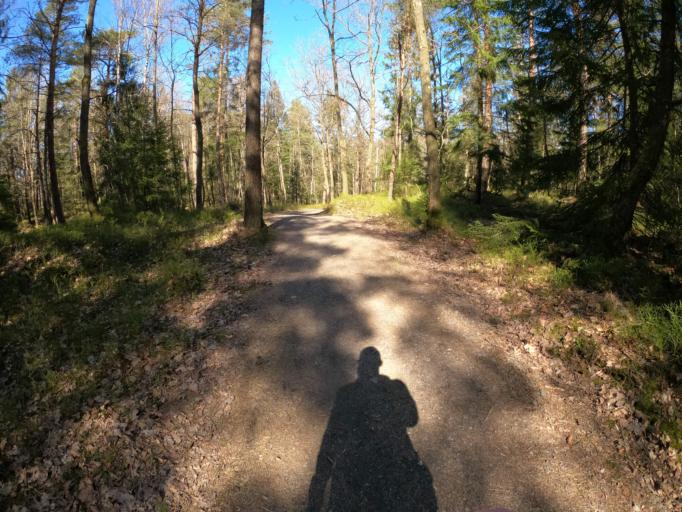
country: SE
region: Vaestra Goetaland
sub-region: Harryda Kommun
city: Molnlycke
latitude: 57.6206
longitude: 12.1101
